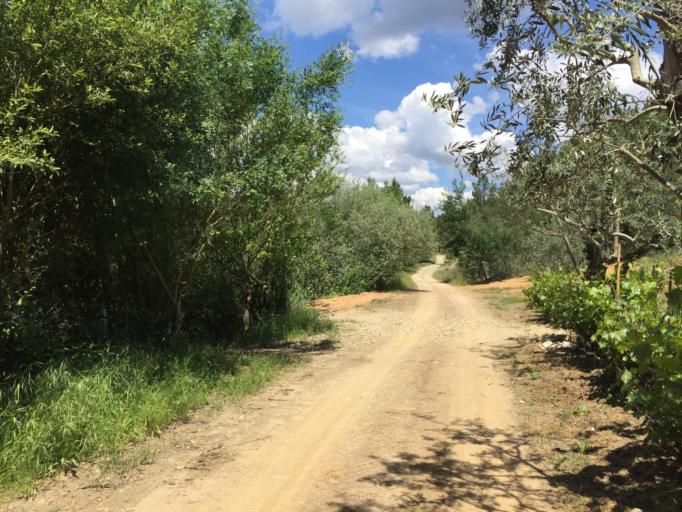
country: PT
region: Coimbra
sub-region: Pampilhosa da Serra
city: Pampilhosa da Serra
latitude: 40.0764
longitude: -7.7865
